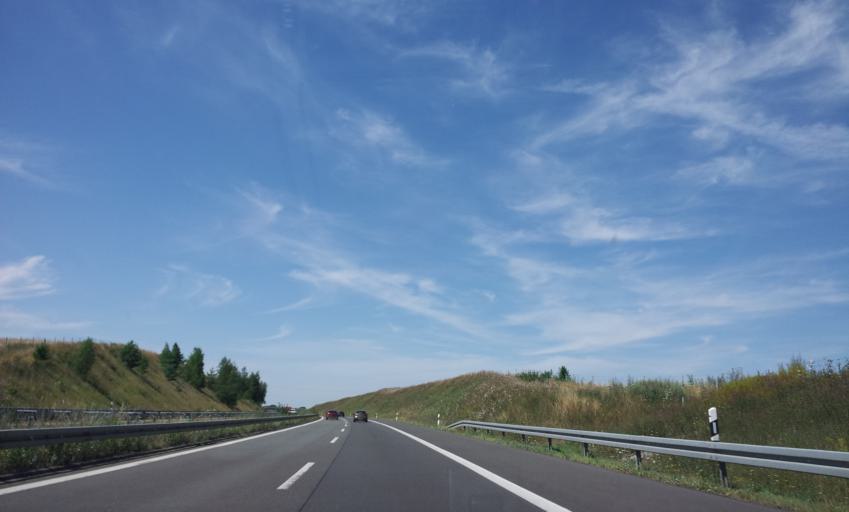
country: DE
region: Mecklenburg-Vorpommern
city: Strasburg
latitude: 53.5299
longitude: 13.7568
